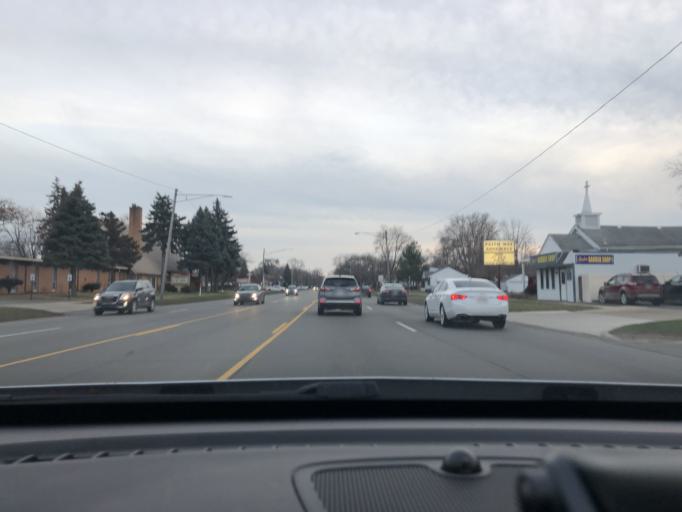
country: US
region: Michigan
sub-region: Wayne County
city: Allen Park
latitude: 42.2557
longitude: -83.2312
